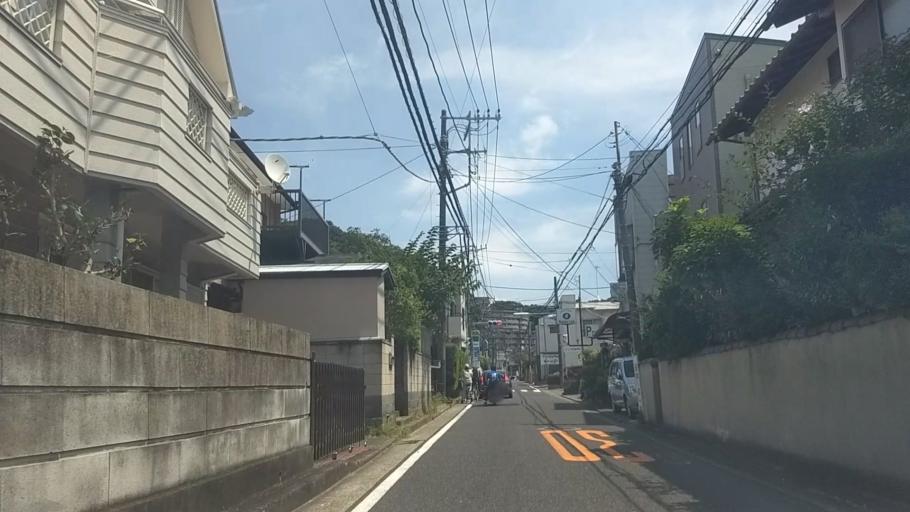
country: JP
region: Kanagawa
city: Kamakura
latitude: 35.3001
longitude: 139.5625
